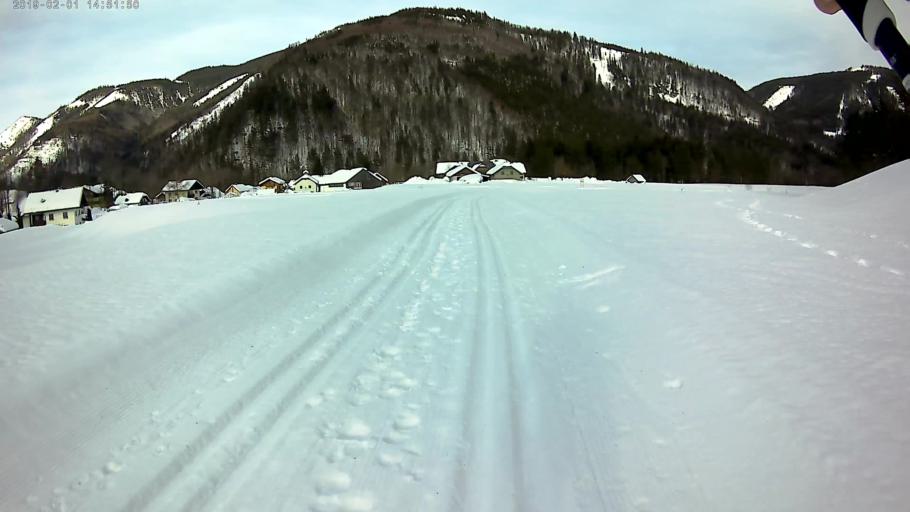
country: AT
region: Salzburg
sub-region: Politischer Bezirk Salzburg-Umgebung
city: Hintersee
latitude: 47.7111
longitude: 13.2888
